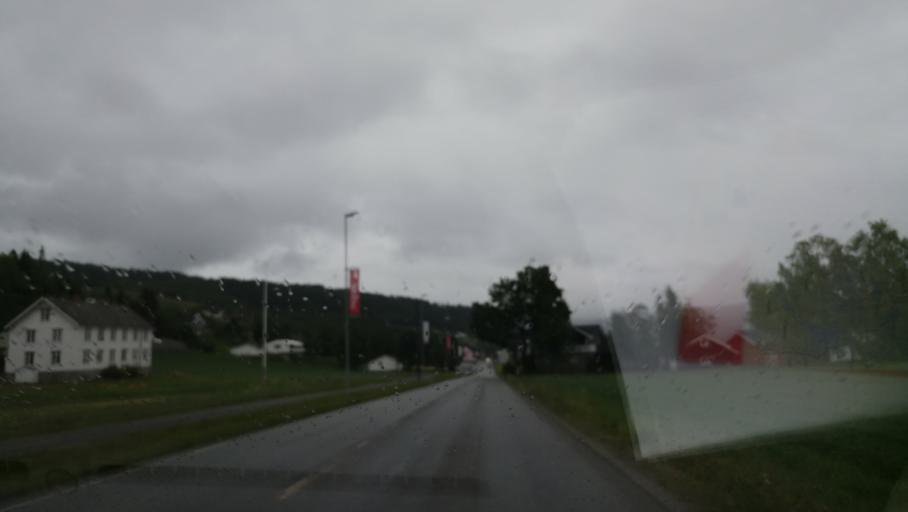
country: NO
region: Sor-Trondelag
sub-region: Selbu
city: Mebonden
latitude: 63.2241
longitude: 11.0328
